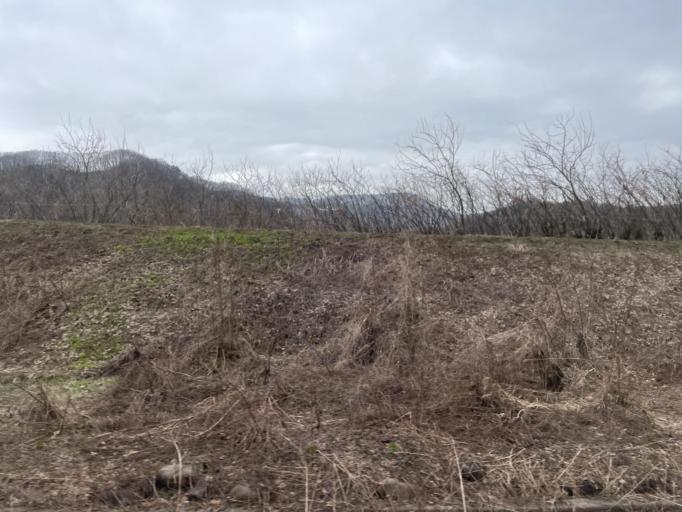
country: JP
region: Gunma
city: Numata
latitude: 36.7269
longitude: 138.9822
